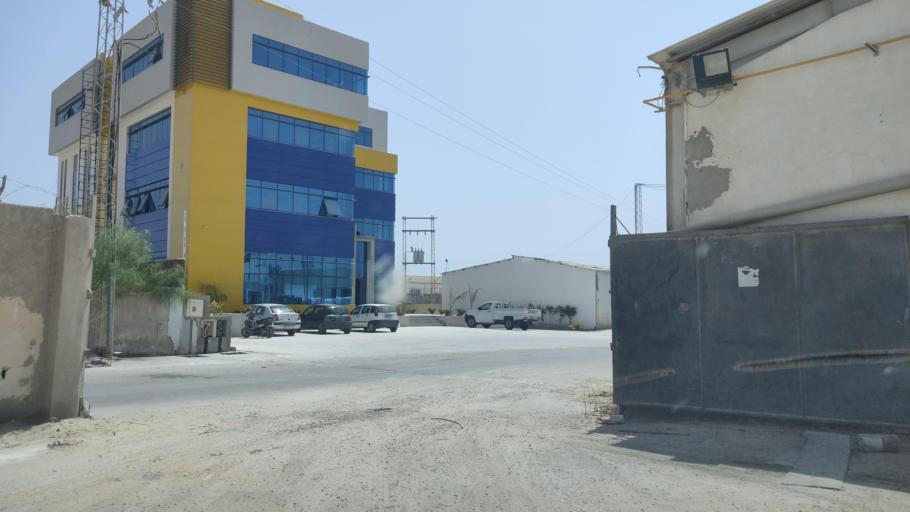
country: TN
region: Safaqis
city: Sfax
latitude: 34.7054
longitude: 10.7250
